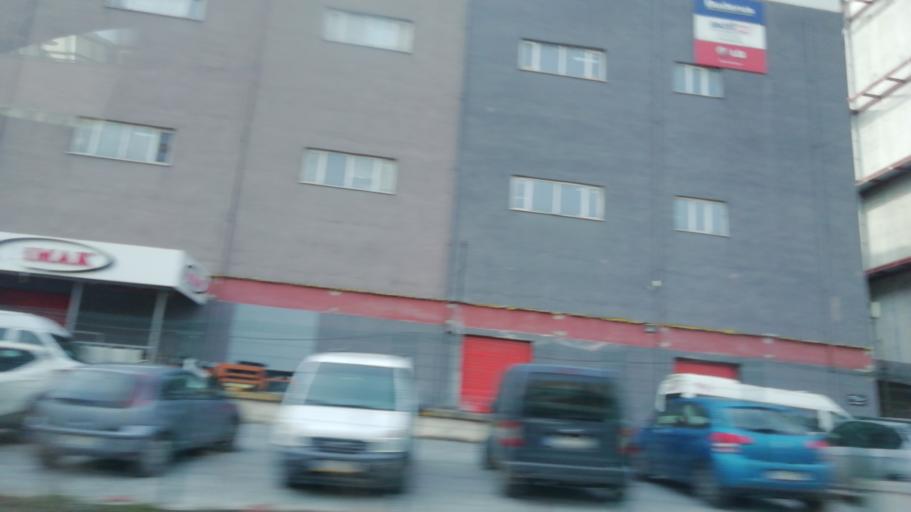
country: TR
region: Istanbul
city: Basaksehir
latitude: 41.0889
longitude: 28.8039
